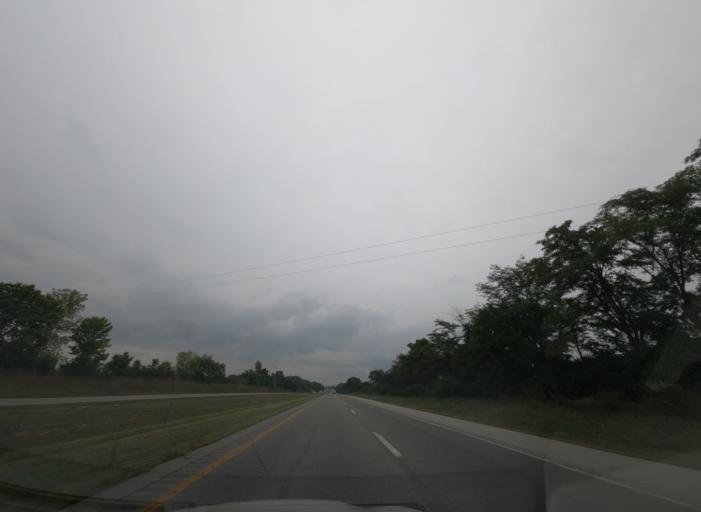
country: US
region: Indiana
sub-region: Morgan County
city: Mooresville
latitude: 39.6423
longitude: -86.4227
